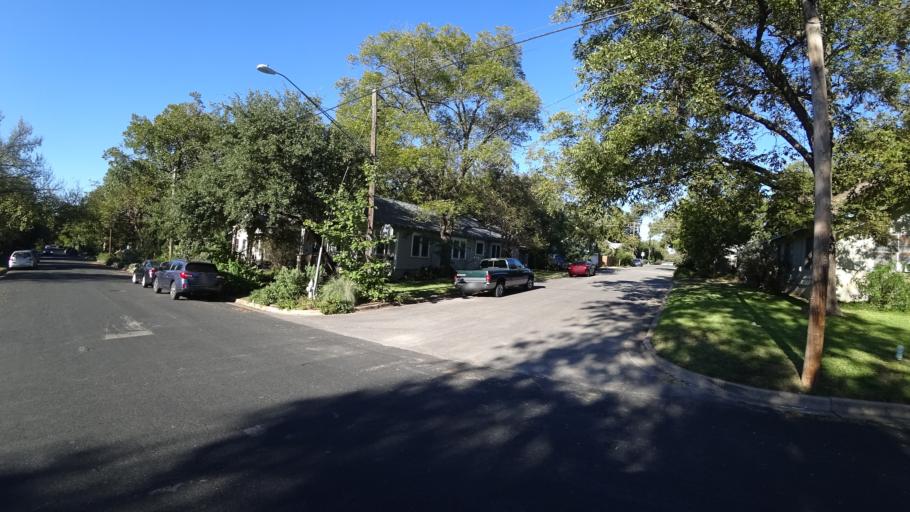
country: US
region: Texas
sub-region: Travis County
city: Austin
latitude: 30.3113
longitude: -97.7230
